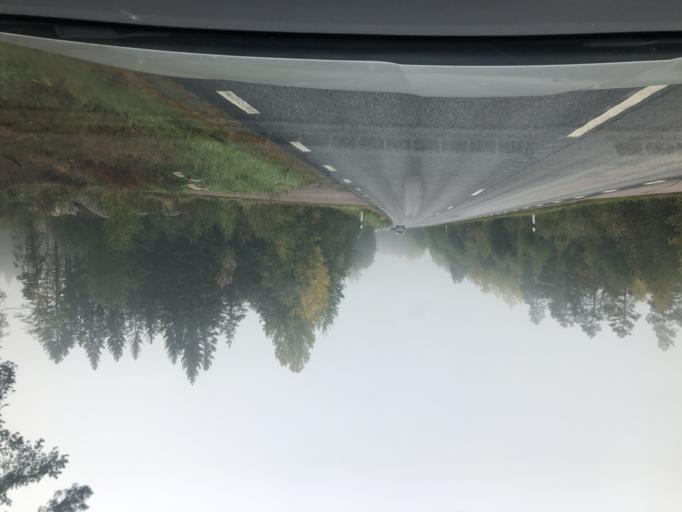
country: SE
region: Uppsala
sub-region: Tierps Kommun
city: Tierp
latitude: 60.3173
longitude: 17.5357
